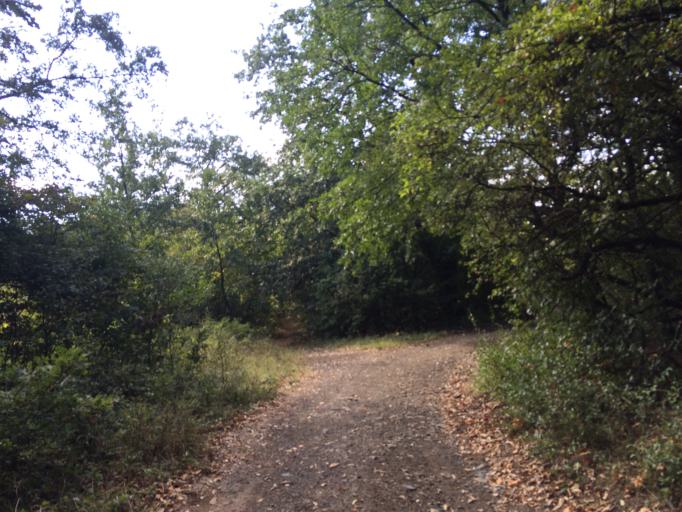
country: HU
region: Pest
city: Nagymaros
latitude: 47.8250
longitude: 18.9455
